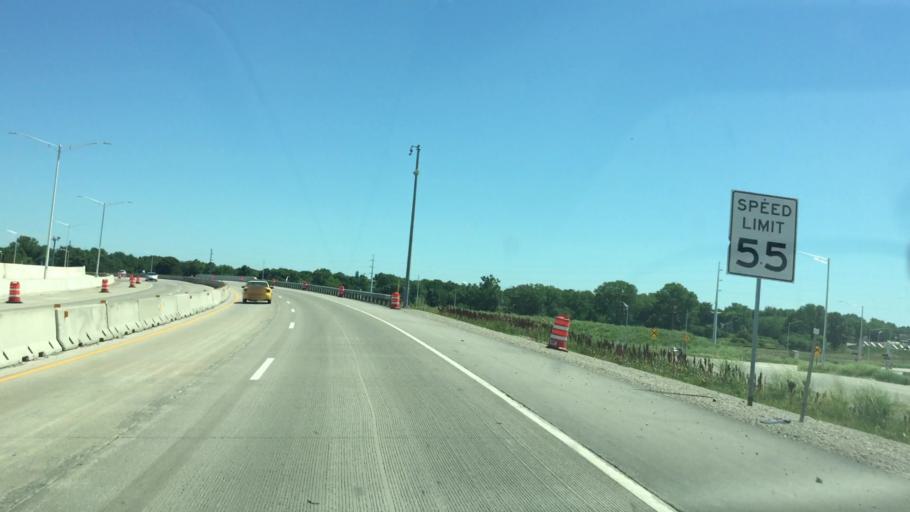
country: US
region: Wisconsin
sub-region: Winnebago County
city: Menasha
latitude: 44.2188
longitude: -88.4512
